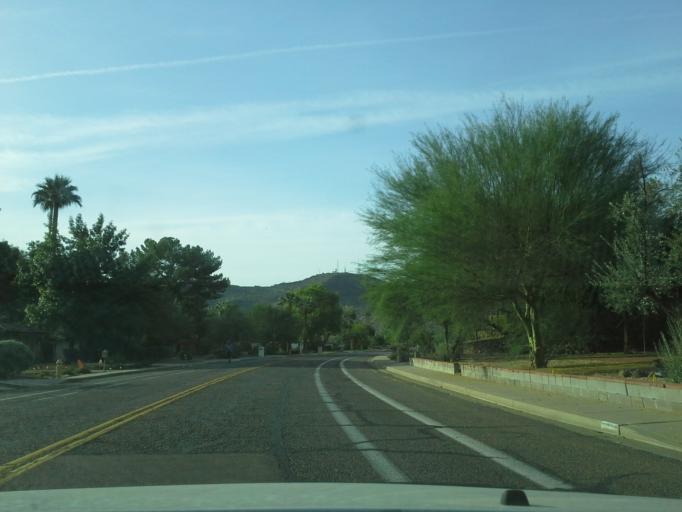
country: US
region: Arizona
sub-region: Maricopa County
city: Glendale
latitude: 33.6144
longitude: -112.0848
